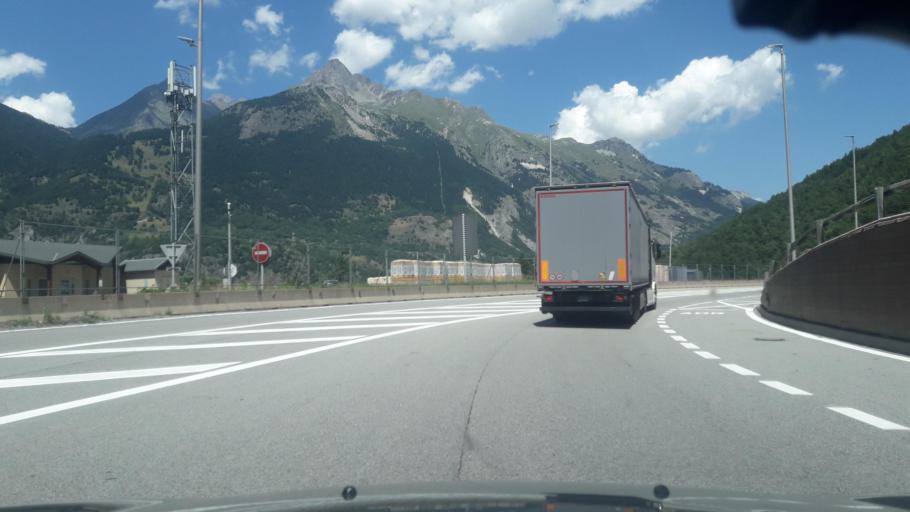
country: FR
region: Rhone-Alpes
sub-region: Departement de la Savoie
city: Modane
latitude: 45.1950
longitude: 6.6743
